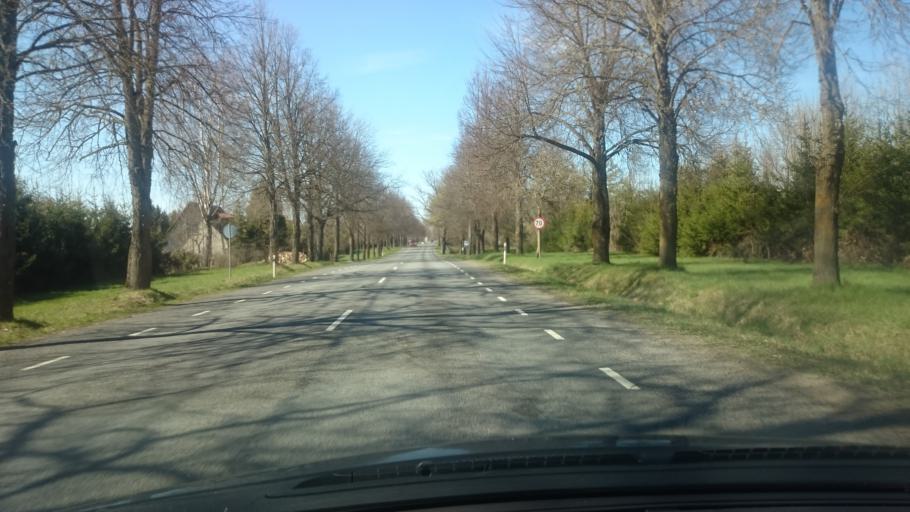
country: EE
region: Polvamaa
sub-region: Polva linn
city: Polva
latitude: 58.1990
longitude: 27.0779
